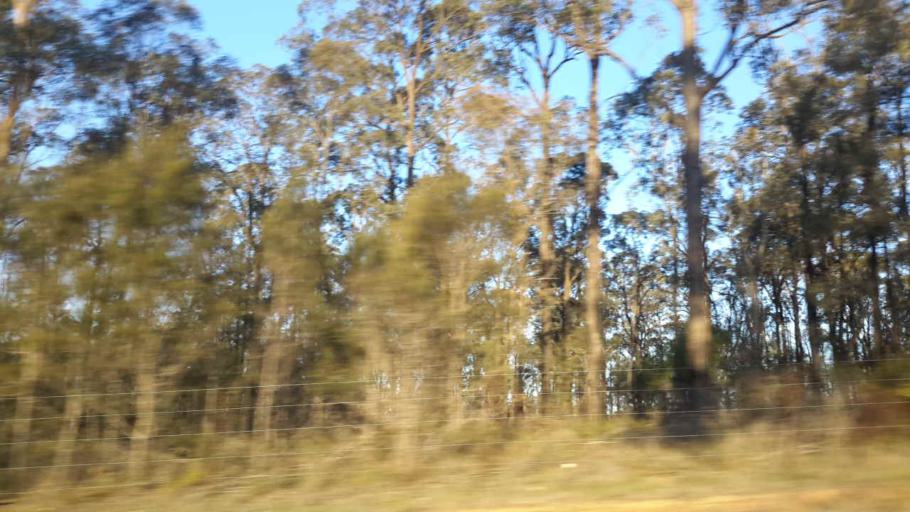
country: AU
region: New South Wales
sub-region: Wollondilly
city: Douglas Park
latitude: -34.2208
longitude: 150.7247
